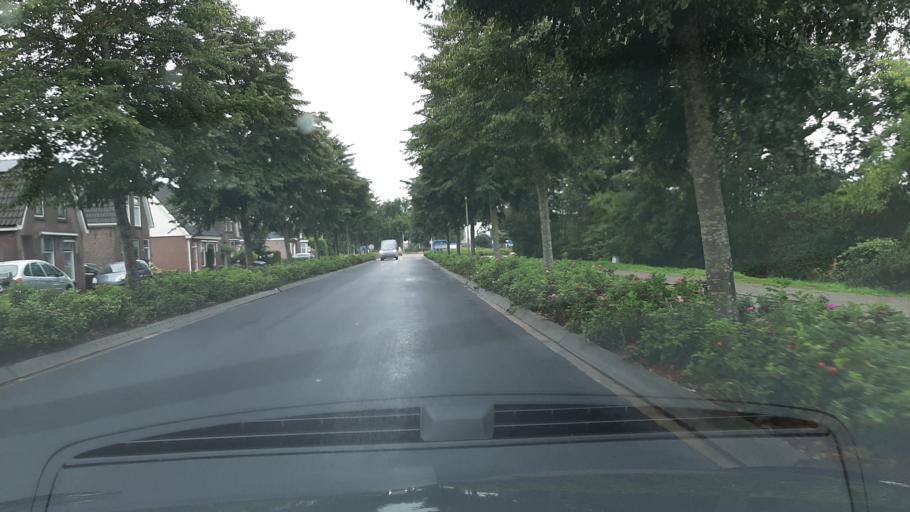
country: NL
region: Friesland
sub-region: Gemeente Weststellingwerf
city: Wolvega
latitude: 52.8872
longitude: 6.0003
